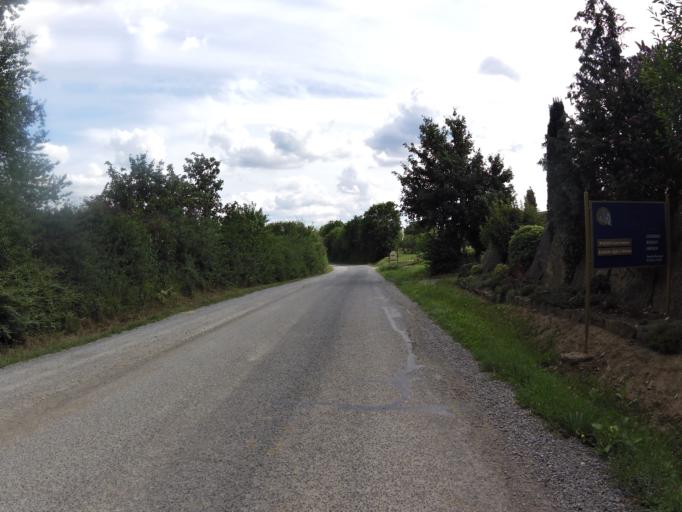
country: DE
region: Bavaria
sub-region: Regierungsbezirk Unterfranken
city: Sommerhausen
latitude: 49.7005
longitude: 10.0371
